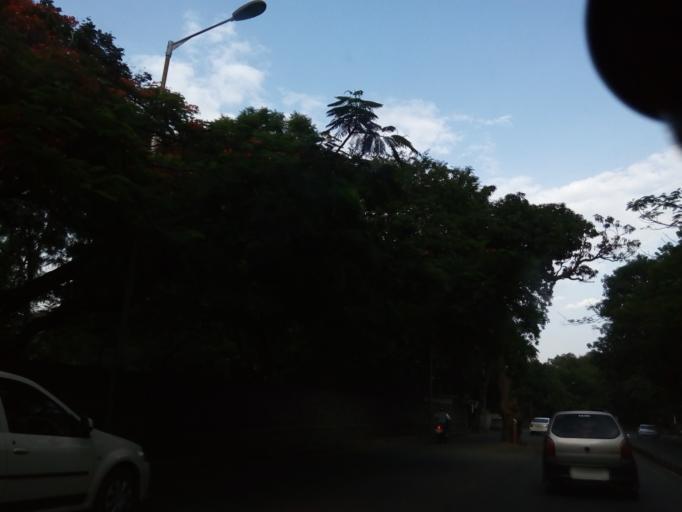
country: IN
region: Karnataka
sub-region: Bangalore Urban
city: Bangalore
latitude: 13.0143
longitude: 77.5867
